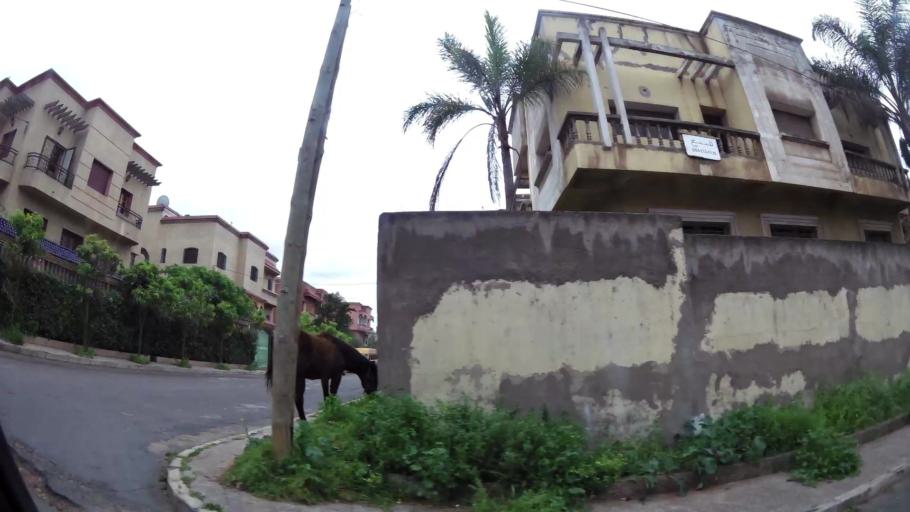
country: MA
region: Grand Casablanca
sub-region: Mediouna
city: Tit Mellil
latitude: 33.5651
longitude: -7.5326
